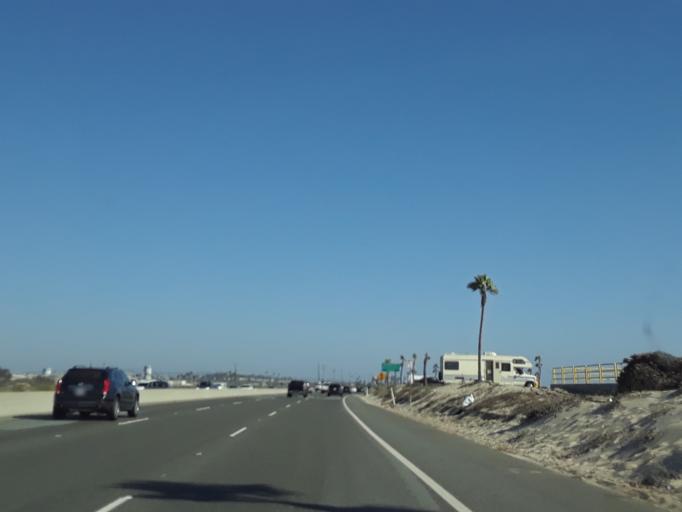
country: US
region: California
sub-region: Orange County
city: Huntington Beach
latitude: 33.6374
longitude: -117.9683
